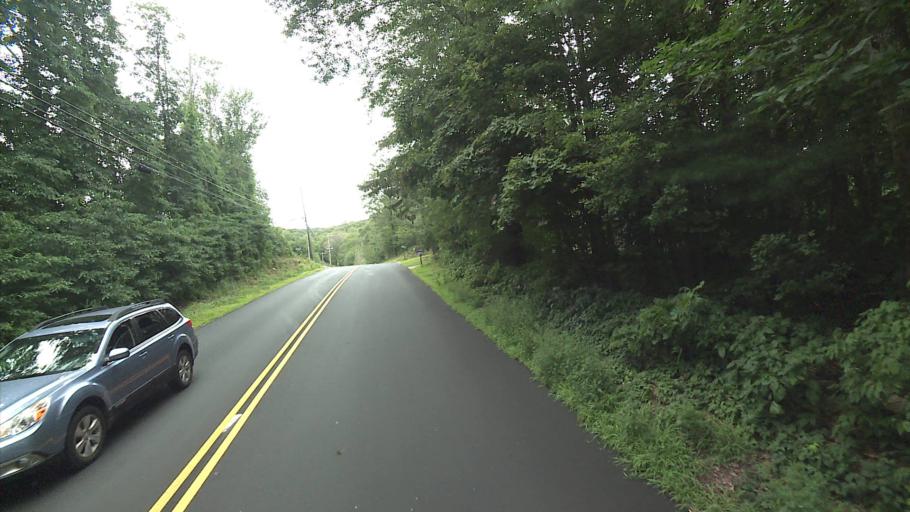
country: US
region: Connecticut
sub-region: Windham County
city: South Woodstock
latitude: 41.9485
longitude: -72.0151
